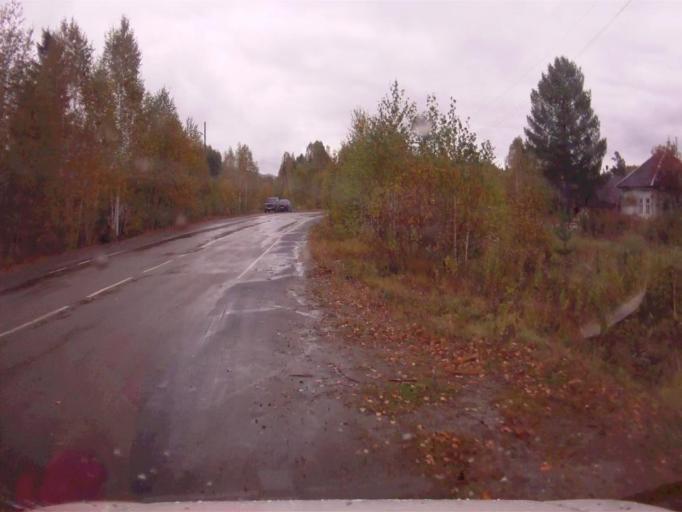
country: RU
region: Chelyabinsk
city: Kyshtym
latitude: 55.8224
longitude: 60.4751
